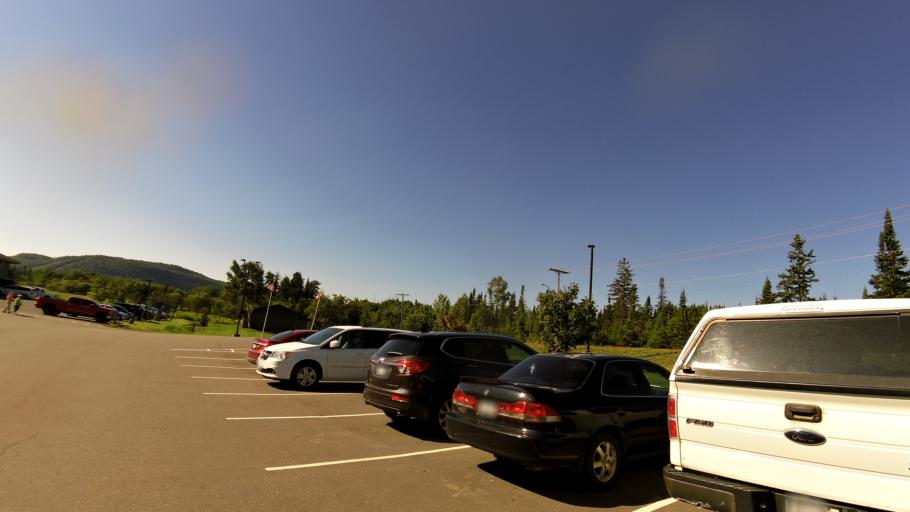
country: CA
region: Ontario
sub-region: Thunder Bay District
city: Thunder Bay
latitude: 48.3158
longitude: -89.3607
